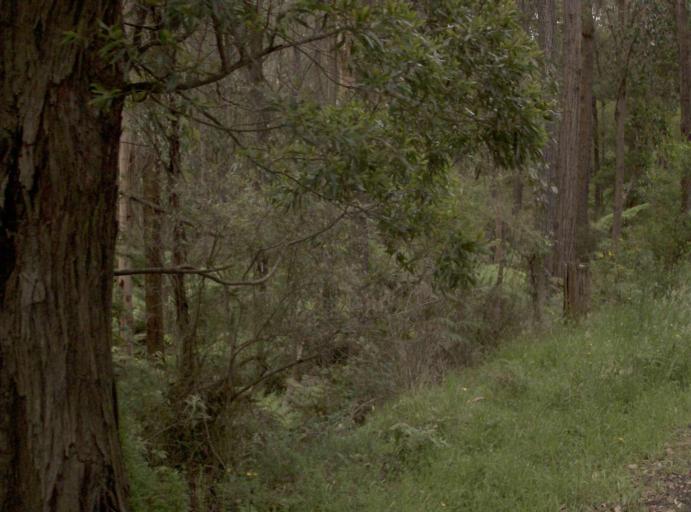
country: AU
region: Victoria
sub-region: Latrobe
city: Moe
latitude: -37.9412
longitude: 146.1163
